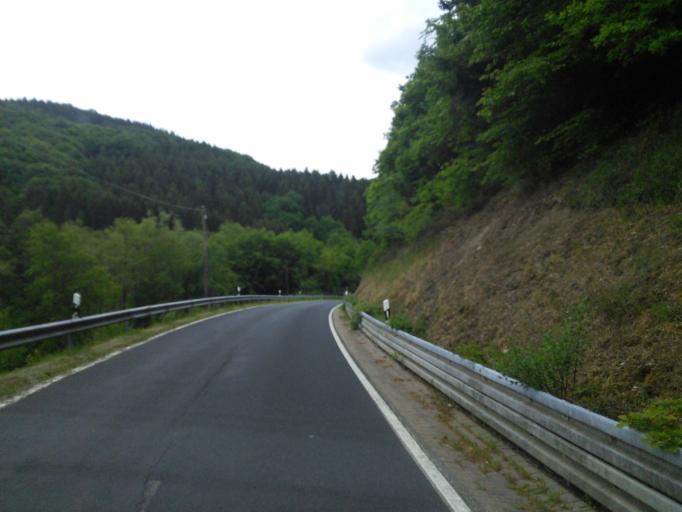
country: DE
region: Rheinland-Pfalz
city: Kirchsahr
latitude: 50.5354
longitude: 6.9064
